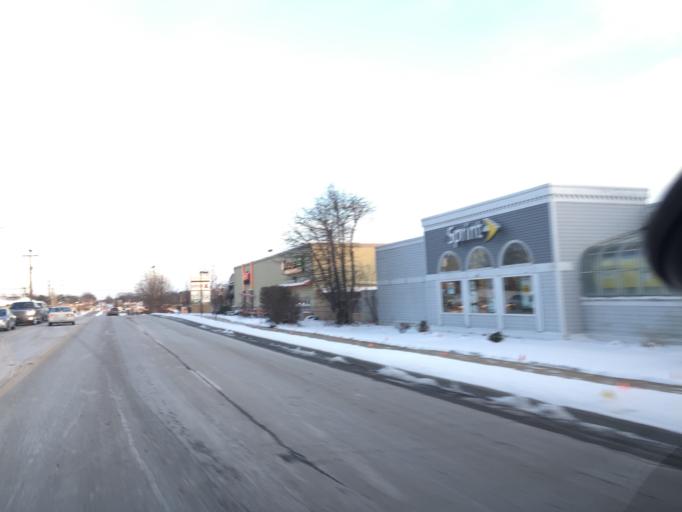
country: US
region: Indiana
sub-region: Monroe County
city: Bloomington
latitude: 39.1643
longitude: -86.5023
